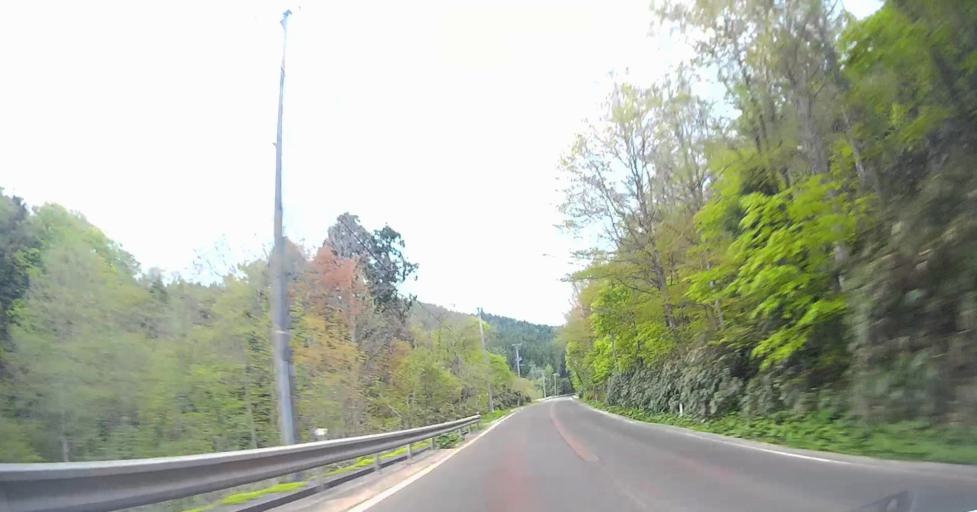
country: JP
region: Aomori
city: Goshogawara
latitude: 41.1017
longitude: 140.5515
